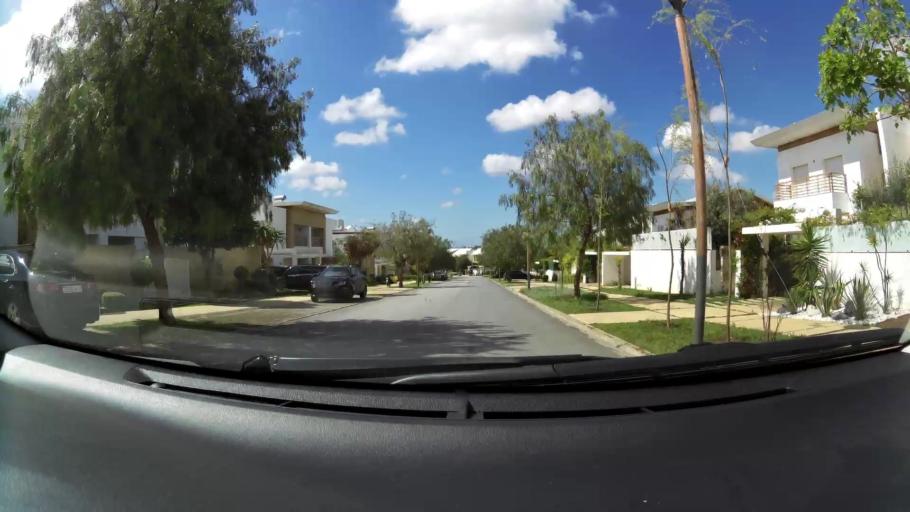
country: MA
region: Grand Casablanca
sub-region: Mediouna
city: Mediouna
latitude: 33.4891
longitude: -7.5832
